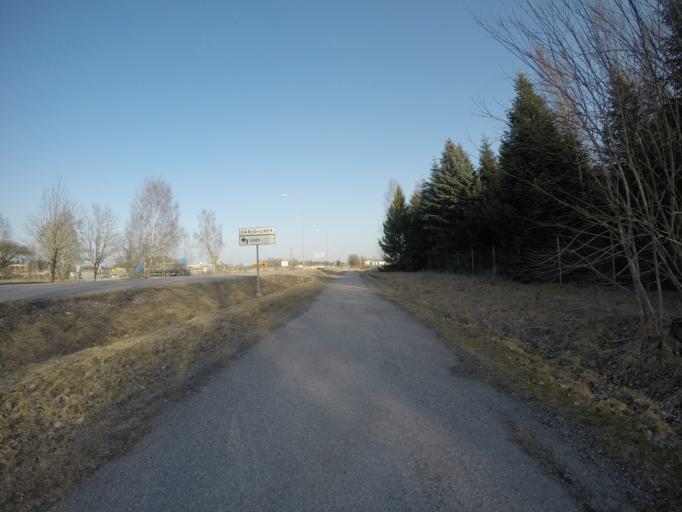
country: SE
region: Vaestmanland
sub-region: Kungsors Kommun
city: Kungsoer
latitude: 59.4247
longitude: 16.1254
